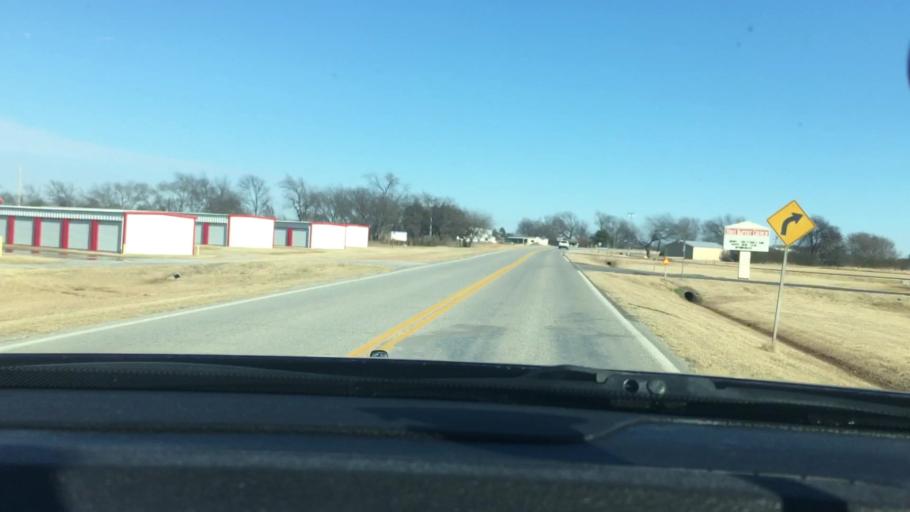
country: US
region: Oklahoma
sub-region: Garvin County
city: Wynnewood
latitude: 34.6487
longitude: -97.1505
